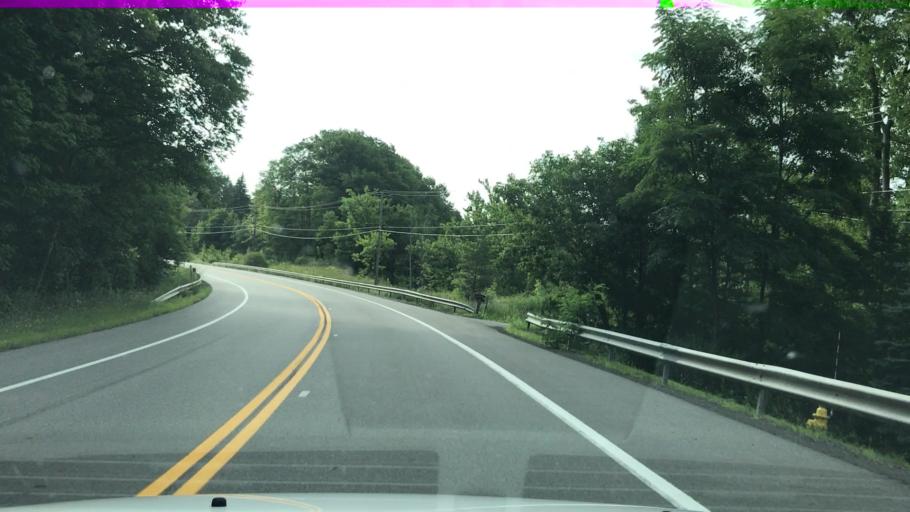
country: US
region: New York
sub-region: Erie County
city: Alden
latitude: 42.8508
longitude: -78.4913
